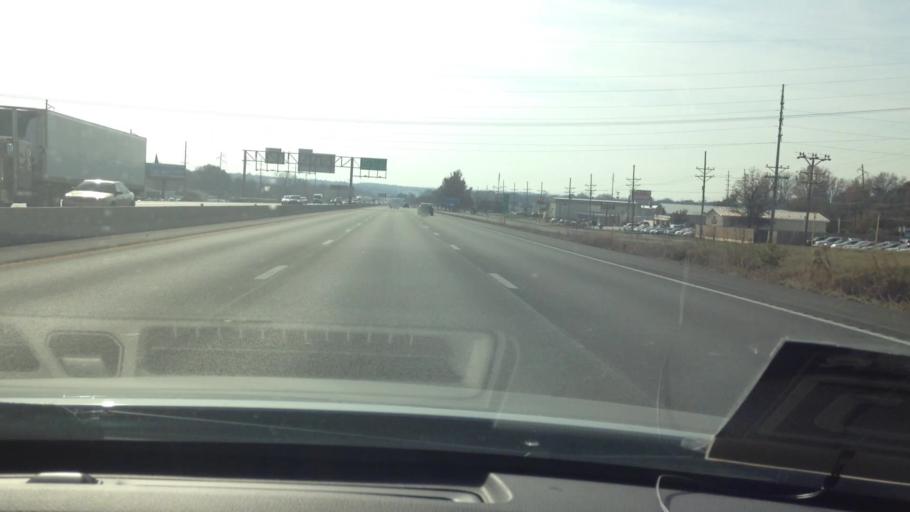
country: US
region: Missouri
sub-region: Jackson County
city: Grandview
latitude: 38.8835
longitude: -94.5258
